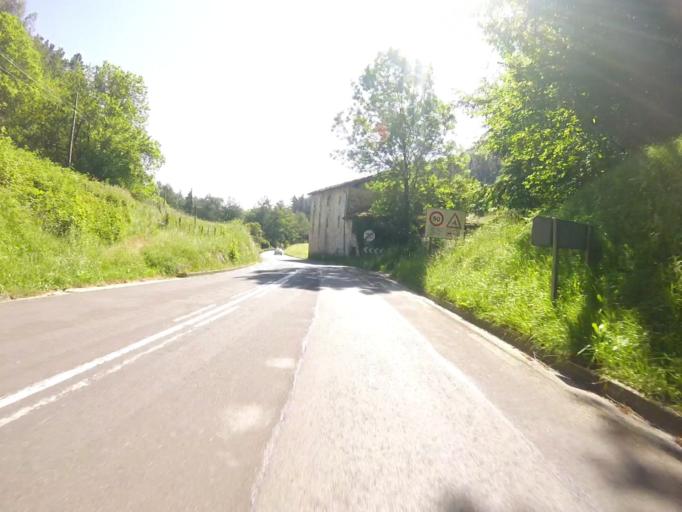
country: ES
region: Basque Country
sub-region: Provincia de Guipuzcoa
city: Albiztur
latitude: 43.1216
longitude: -2.1515
